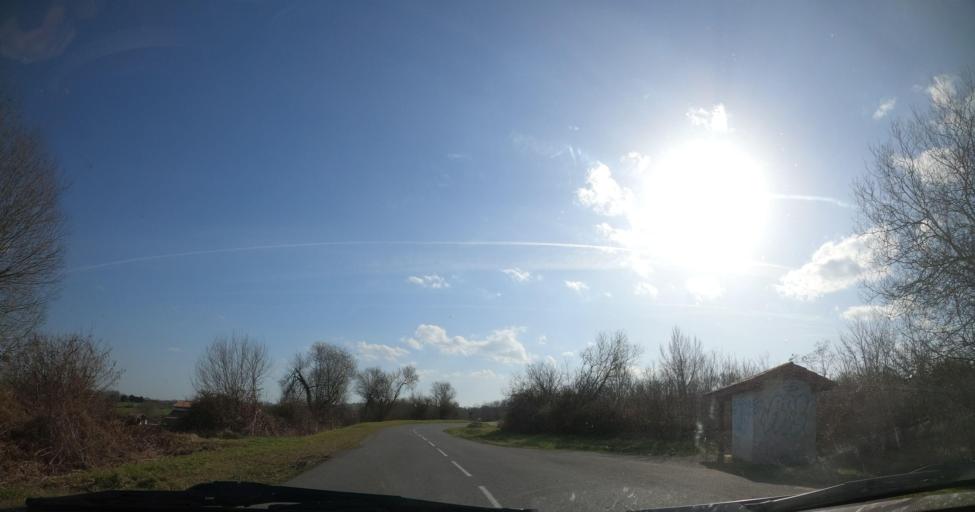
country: FR
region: Aquitaine
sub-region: Departement des Pyrenees-Atlantiques
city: Briscous
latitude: 43.4475
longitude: -1.3708
